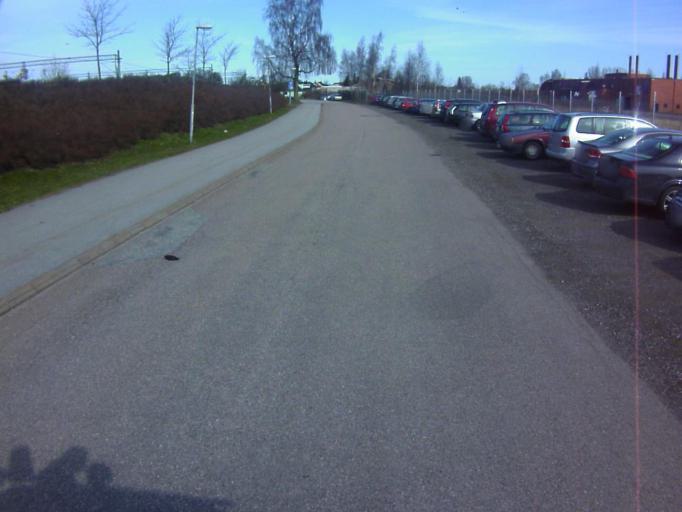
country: SE
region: Skane
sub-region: Kavlinge Kommun
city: Kaevlinge
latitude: 55.7935
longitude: 13.1125
